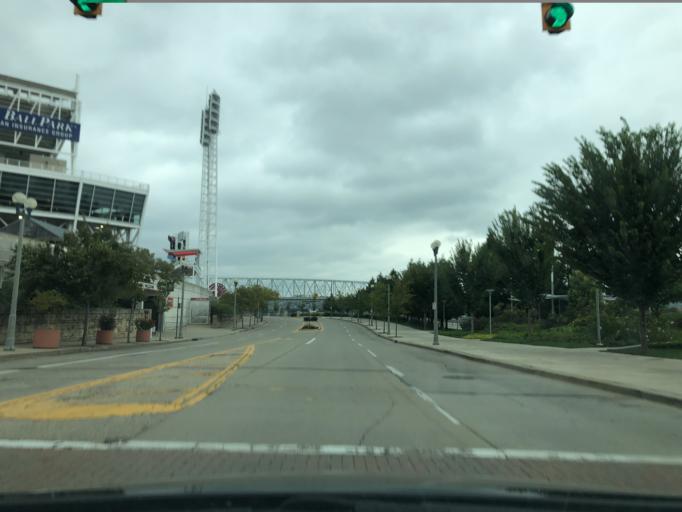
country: US
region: Kentucky
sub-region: Kenton County
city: Covington
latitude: 39.0960
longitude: -84.5087
